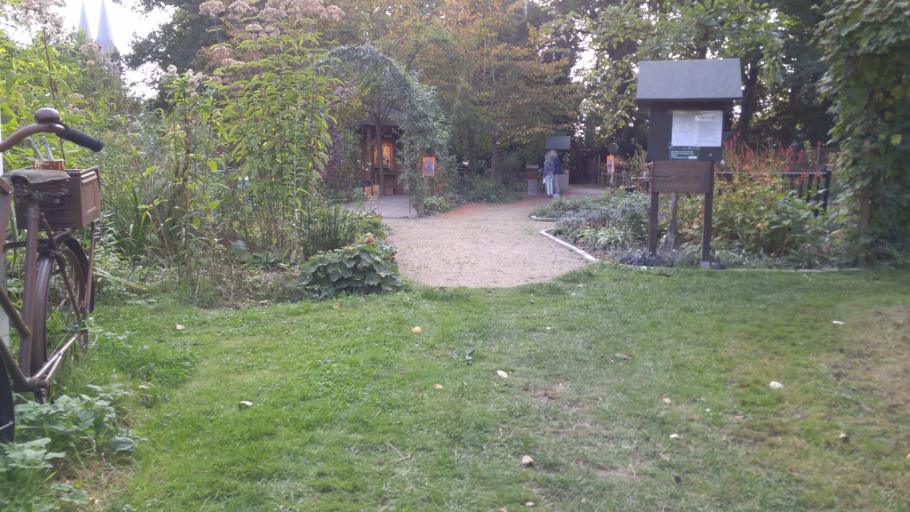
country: NL
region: North Brabant
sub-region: Gemeente Geldrop-Mierlo
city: Geldrop
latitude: 51.4246
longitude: 5.5577
